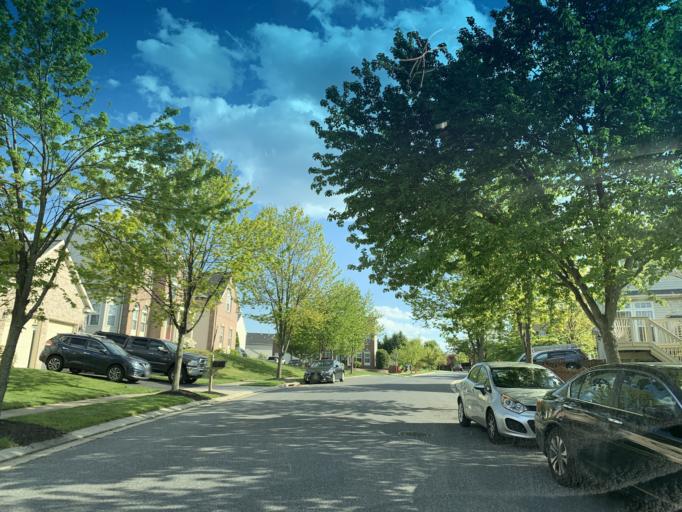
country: US
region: Maryland
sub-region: Baltimore County
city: White Marsh
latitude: 39.4059
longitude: -76.4318
